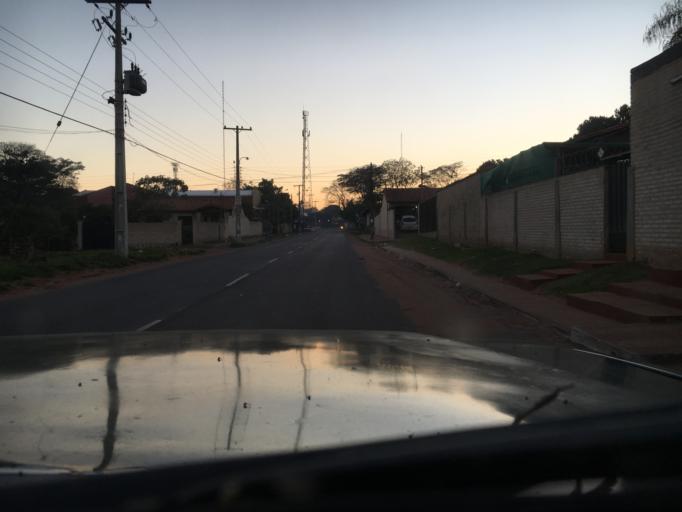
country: PY
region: Central
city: Villa Elisa
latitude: -25.3715
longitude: -57.5862
